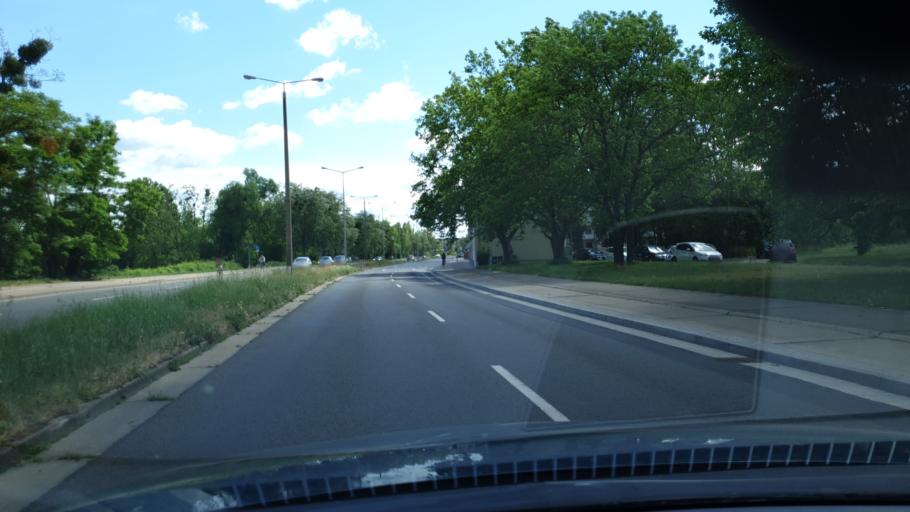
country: DE
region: Saxony-Anhalt
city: Dessau
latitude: 51.8188
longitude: 12.2496
